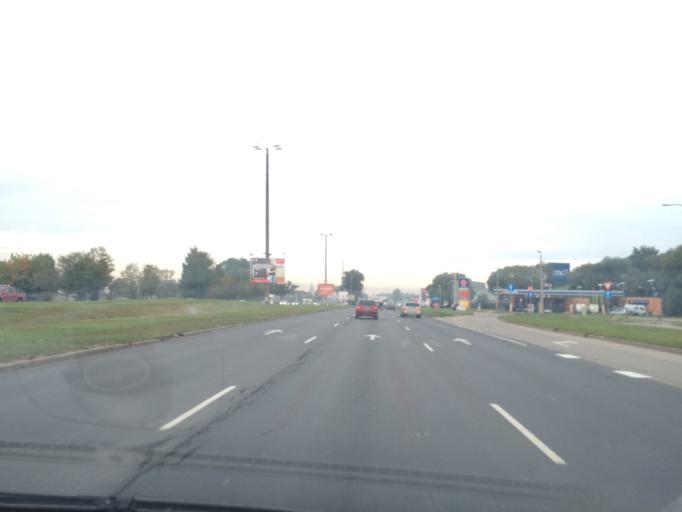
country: LV
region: Riga
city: Riga
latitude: 56.9273
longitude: 24.1581
